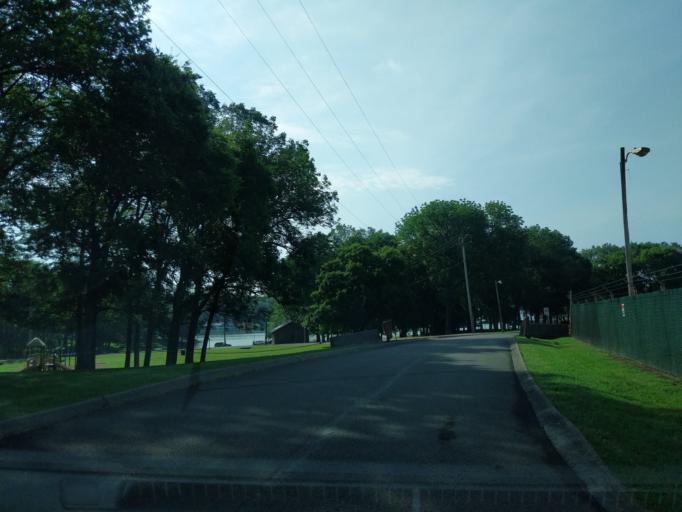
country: US
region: Tennessee
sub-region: Sumner County
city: Hendersonville
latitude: 36.2980
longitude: -86.6525
